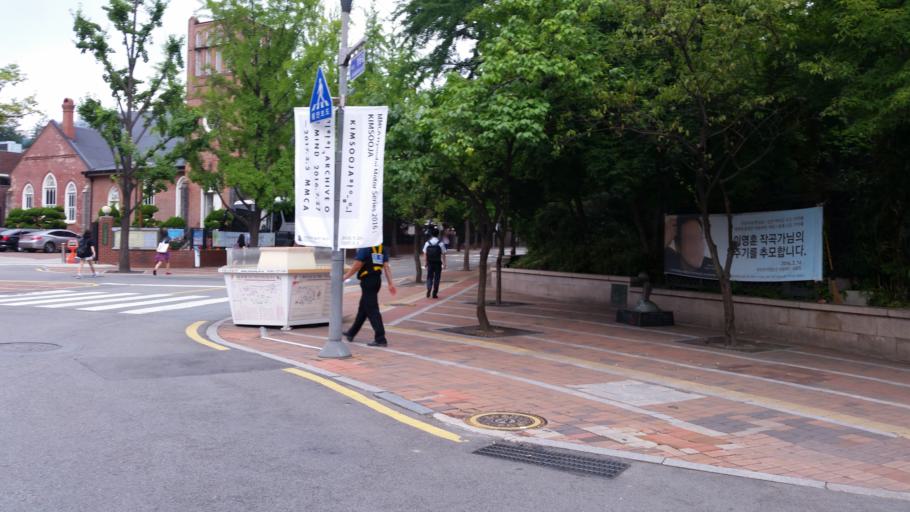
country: KR
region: Seoul
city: Seoul
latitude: 37.5653
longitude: 126.9735
